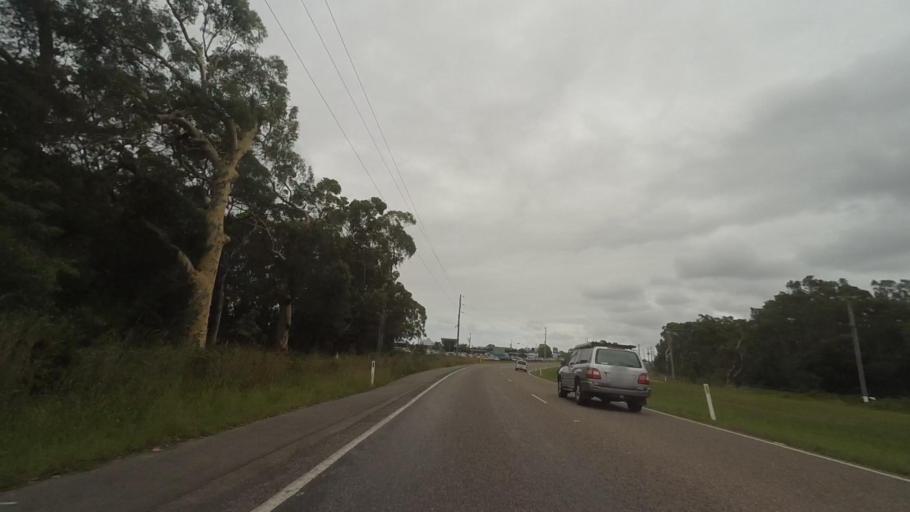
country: AU
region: New South Wales
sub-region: Wyong Shire
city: Buff Point
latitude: -33.1951
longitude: 151.5266
